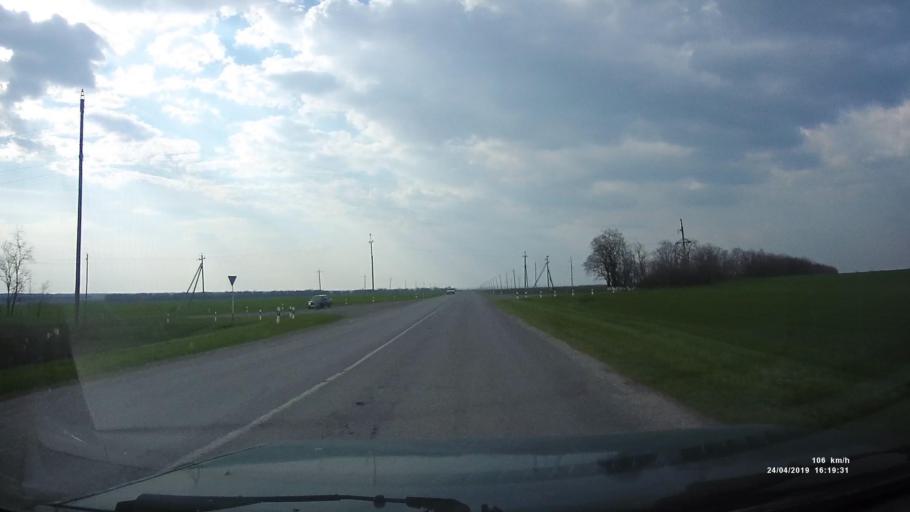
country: RU
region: Rostov
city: Sovetskoye
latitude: 46.7825
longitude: 42.0948
